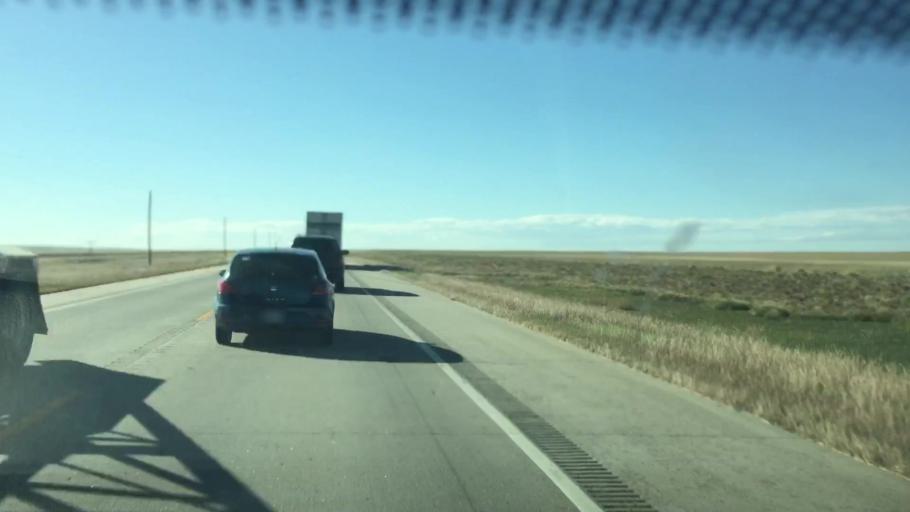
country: US
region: Colorado
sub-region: Kiowa County
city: Eads
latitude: 38.8334
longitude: -103.0577
